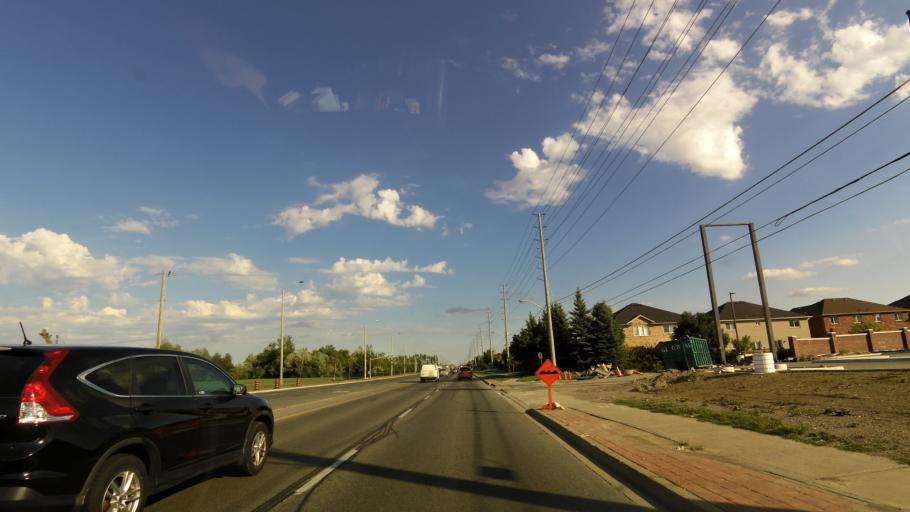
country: CA
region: Ontario
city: Brampton
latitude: 43.6905
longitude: -79.8144
